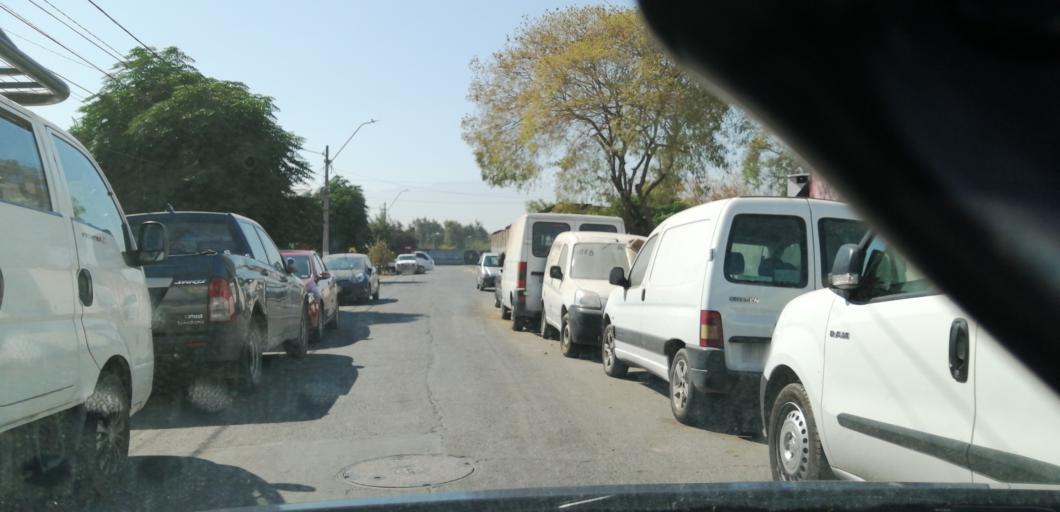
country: CL
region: Santiago Metropolitan
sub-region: Provincia de Santiago
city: Lo Prado
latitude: -33.4430
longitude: -70.7502
